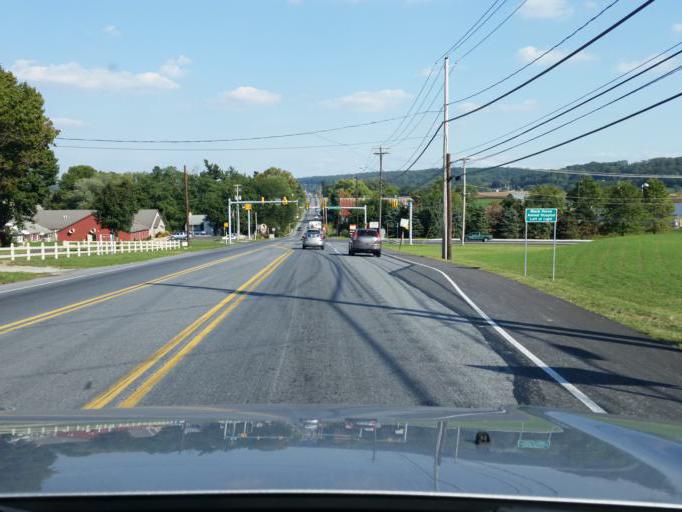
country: US
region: Pennsylvania
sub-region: Lancaster County
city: Gap
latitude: 39.9956
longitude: -76.0445
